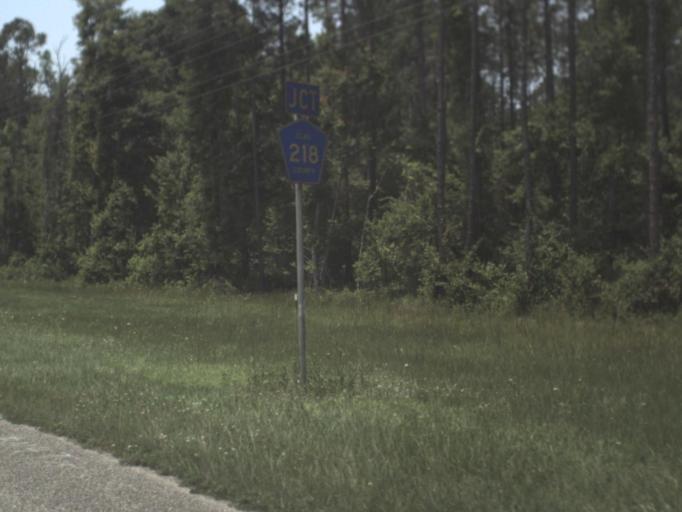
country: US
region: Florida
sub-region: Baker County
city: Macclenny
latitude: 30.1558
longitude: -82.0315
